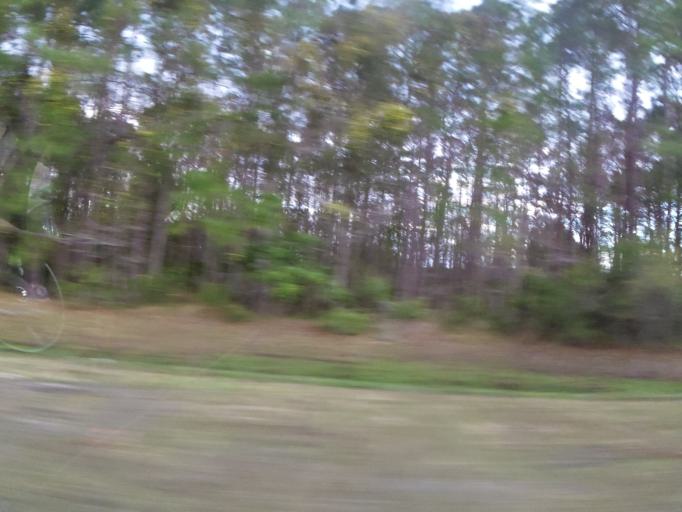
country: US
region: Florida
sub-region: Saint Johns County
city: Fruit Cove
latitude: 30.1863
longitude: -81.5762
